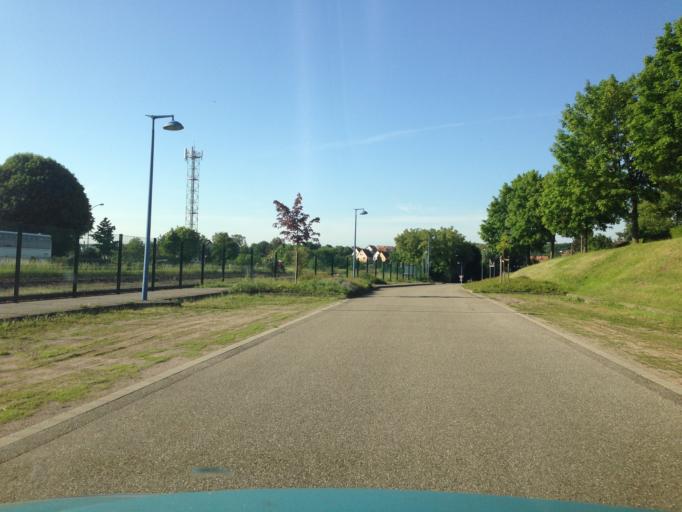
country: FR
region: Alsace
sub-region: Departement du Bas-Rhin
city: Ingwiller
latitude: 48.8713
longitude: 7.4765
